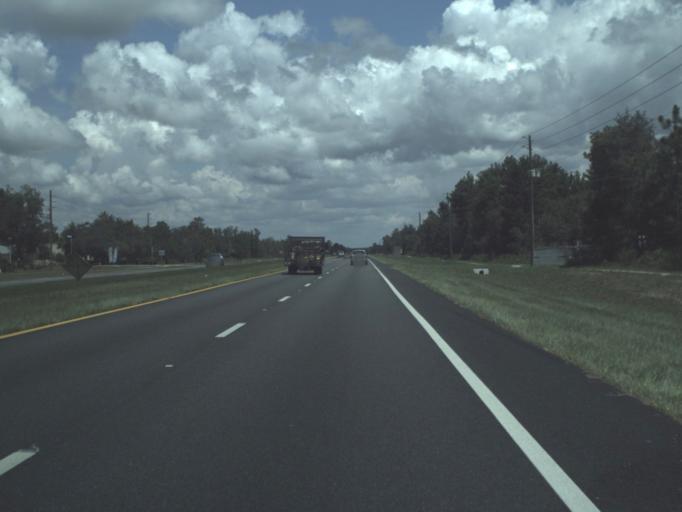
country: US
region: Florida
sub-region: Hernando County
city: North Weeki Wachee
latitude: 28.5687
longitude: -82.5585
